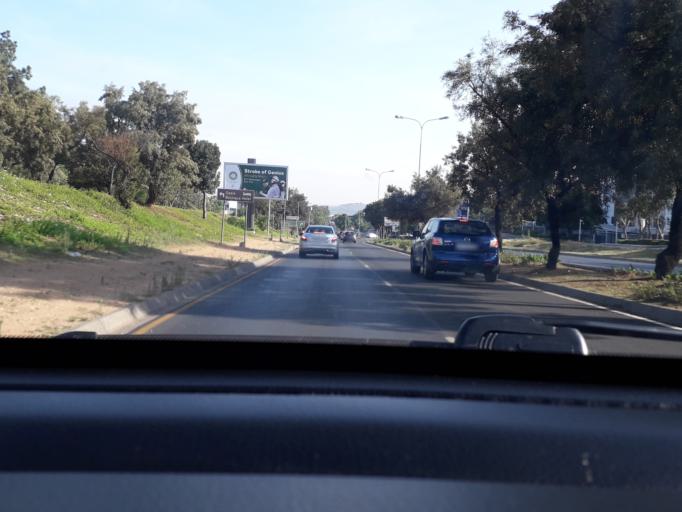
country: ZA
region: Gauteng
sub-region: City of Johannesburg Metropolitan Municipality
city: Midrand
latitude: -26.0567
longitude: 28.0590
